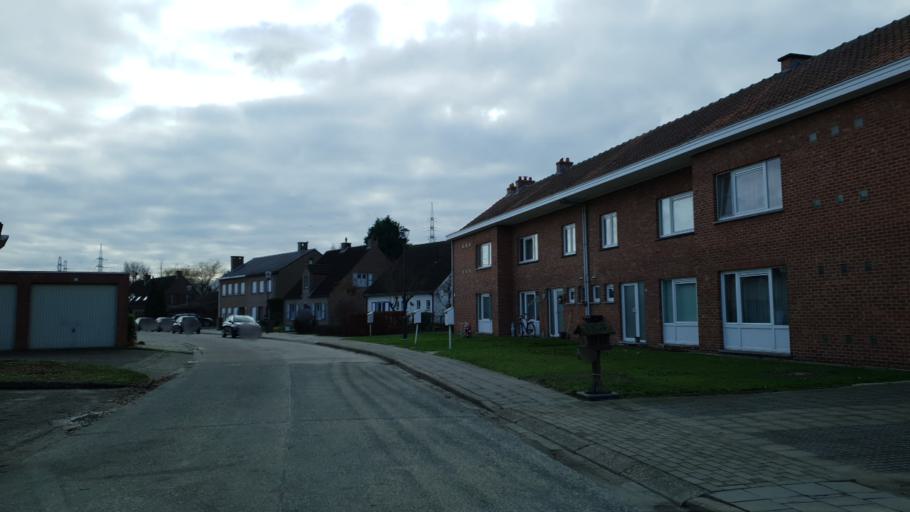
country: BE
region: Flanders
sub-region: Provincie Antwerpen
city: Lier
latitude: 51.1373
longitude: 4.5527
